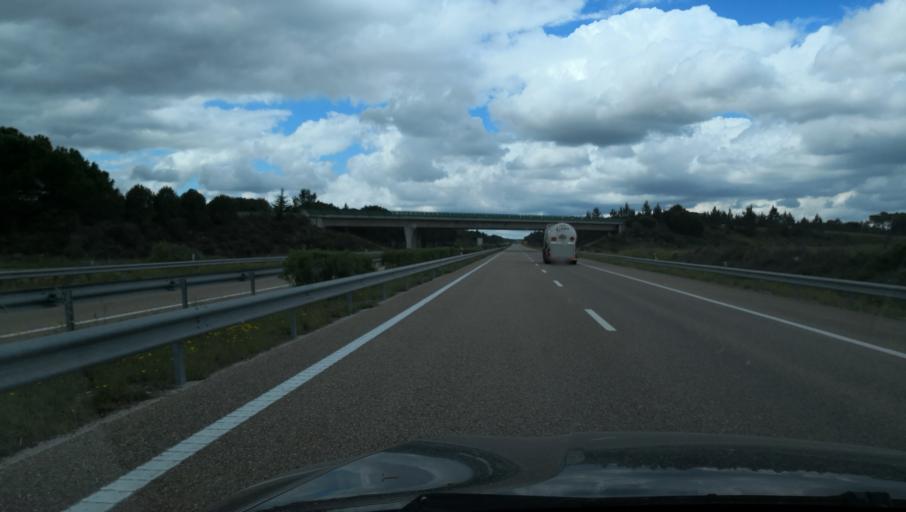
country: PT
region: Evora
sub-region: Vendas Novas
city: Vendas Novas
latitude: 38.6191
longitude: -8.6538
